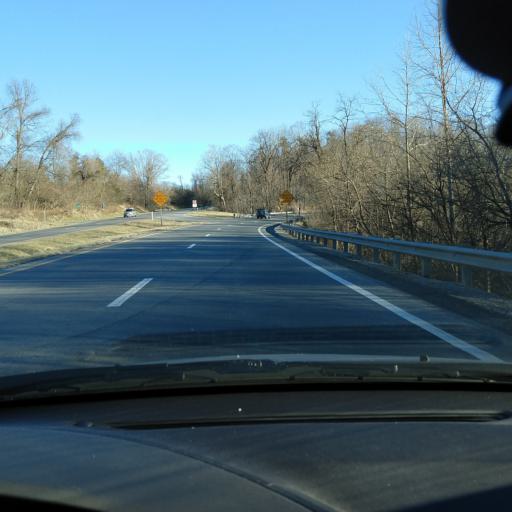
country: US
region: Virginia
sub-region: Botetourt County
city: Blue Ridge
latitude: 37.3692
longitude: -79.6956
